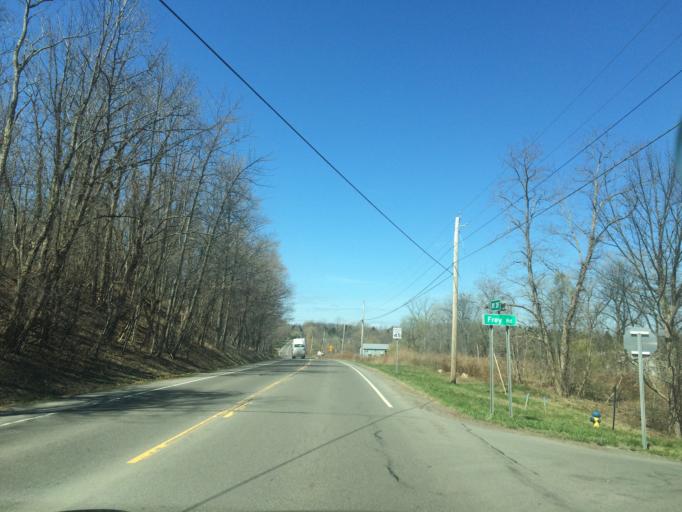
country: US
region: New York
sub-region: Wayne County
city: Macedon
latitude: 43.0944
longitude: -77.3422
